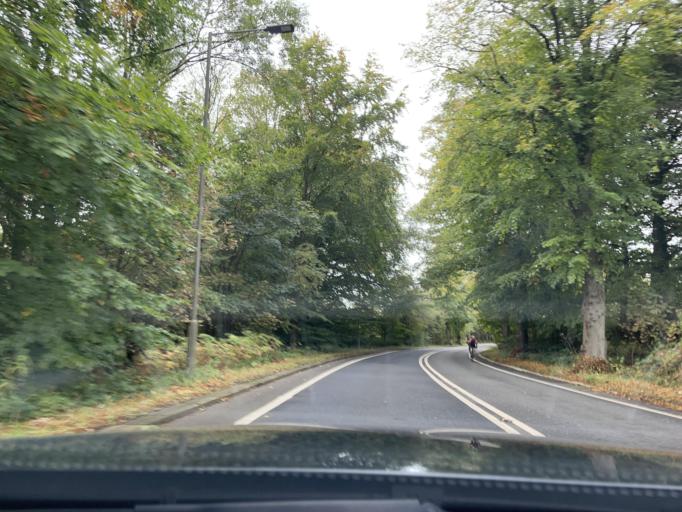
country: GB
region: England
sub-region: Sheffield
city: Oughtibridge
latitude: 53.3823
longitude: -1.5531
